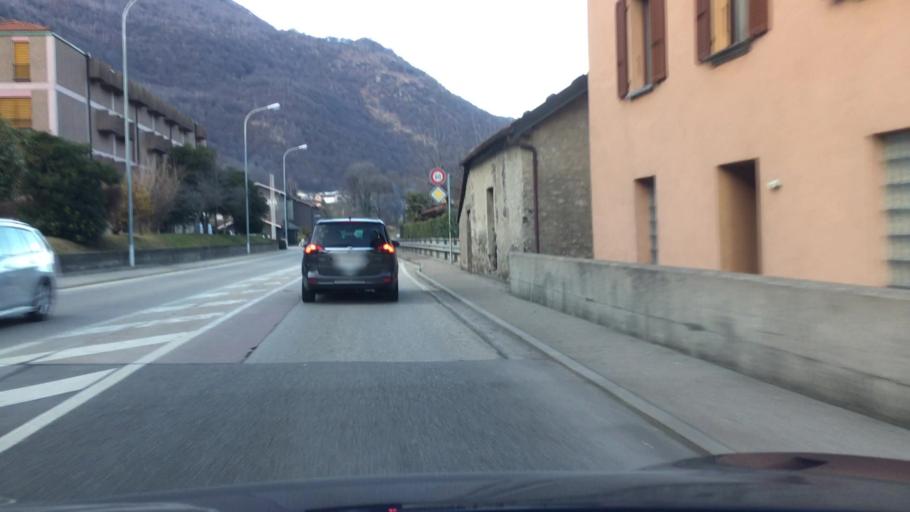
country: CH
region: Ticino
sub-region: Lugano District
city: Gravesano
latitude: 46.0861
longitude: 8.9200
